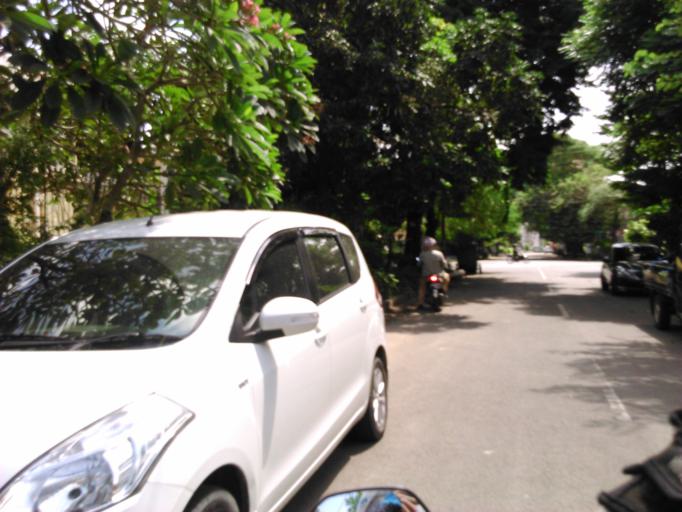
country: ID
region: East Java
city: Jagirsidosermo
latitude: -7.2909
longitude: 112.7409
